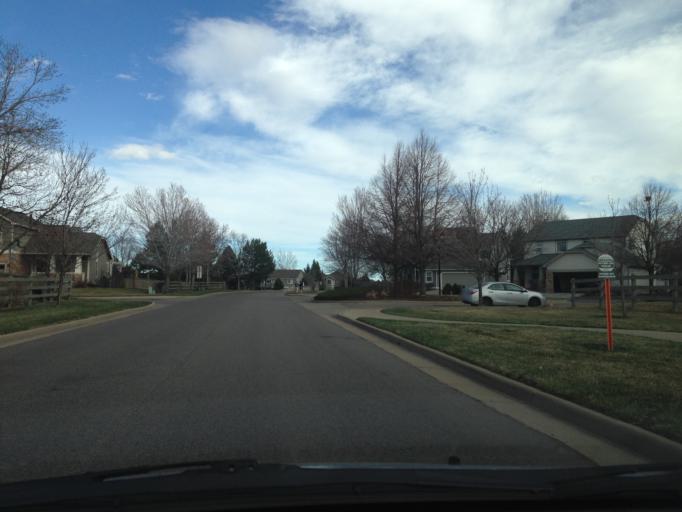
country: US
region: Colorado
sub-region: Boulder County
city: Louisville
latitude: 39.9981
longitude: -105.1212
